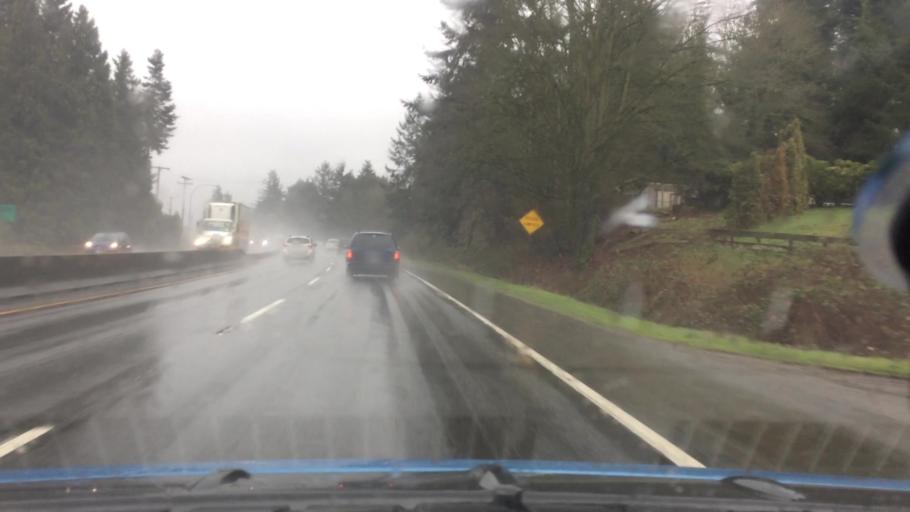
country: CA
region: British Columbia
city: North Saanich
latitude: 48.5684
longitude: -123.3990
